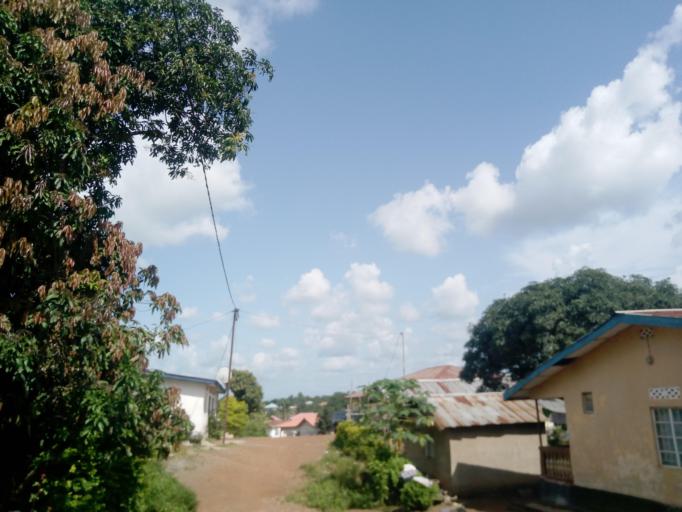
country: SL
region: Northern Province
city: Makeni
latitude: 8.9018
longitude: -12.0306
